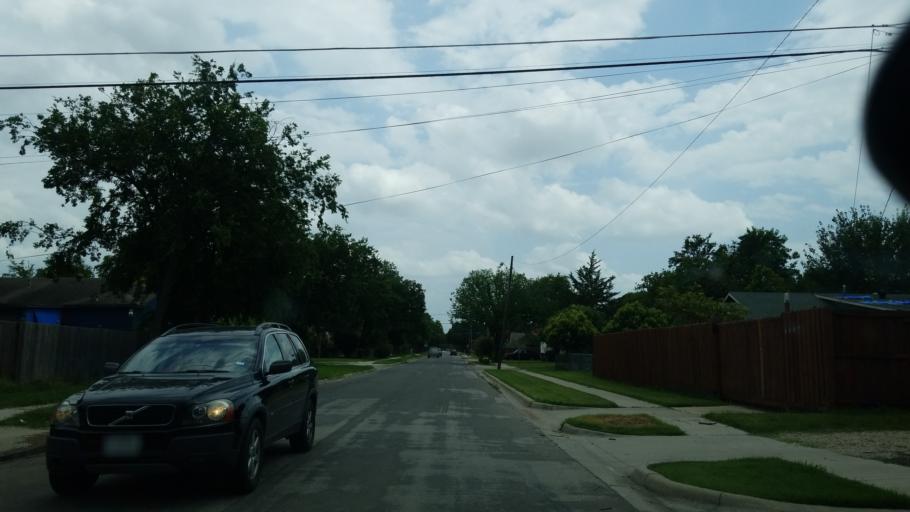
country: US
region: Texas
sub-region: Dallas County
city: University Park
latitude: 32.8728
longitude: -96.8587
